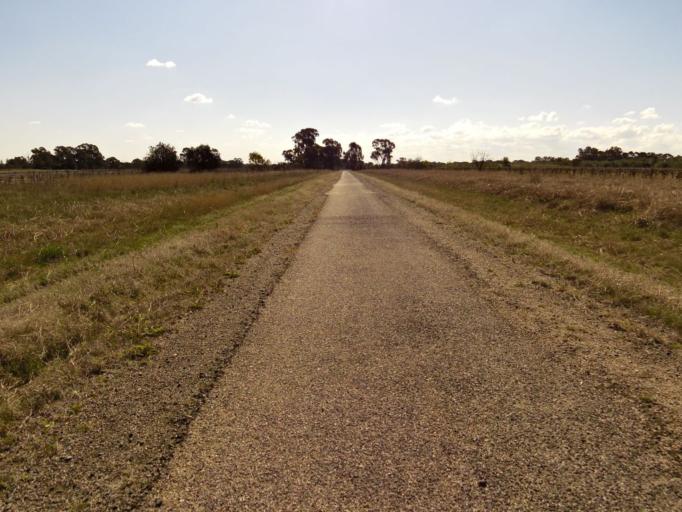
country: AU
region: New South Wales
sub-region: Corowa Shire
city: Corowa
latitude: -36.0428
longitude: 146.4556
